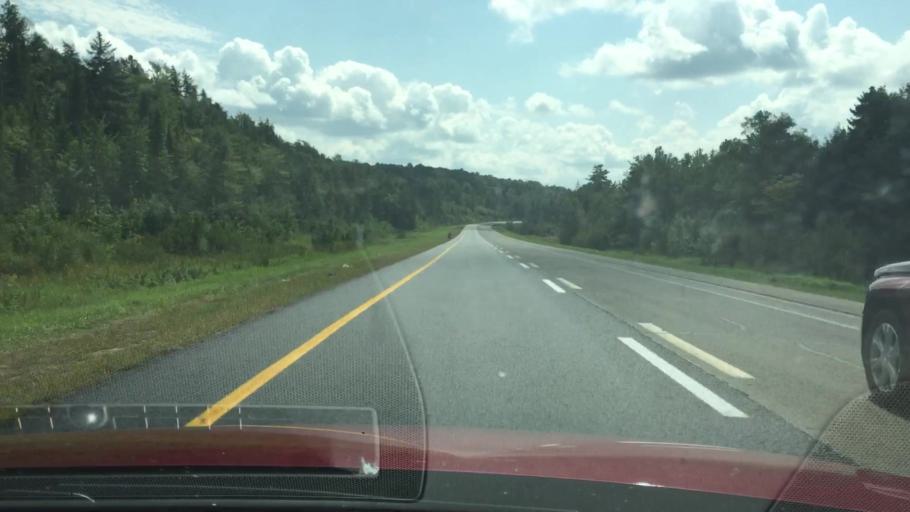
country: US
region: Maine
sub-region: Penobscot County
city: Medway
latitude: 45.7163
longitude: -68.4757
